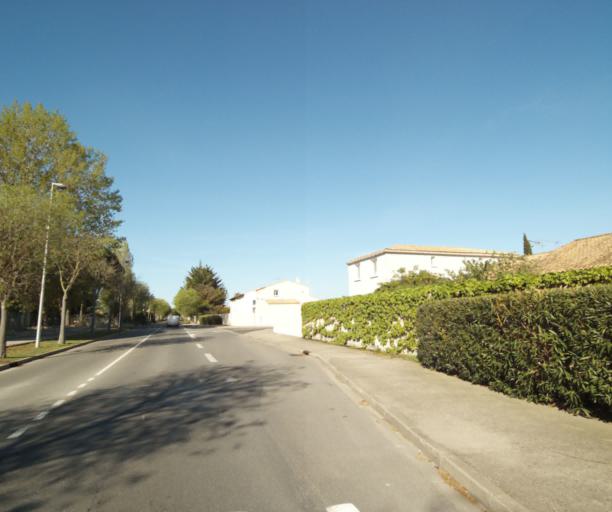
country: FR
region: Languedoc-Roussillon
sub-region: Departement de l'Herault
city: Lattes
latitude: 43.5738
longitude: 3.9093
